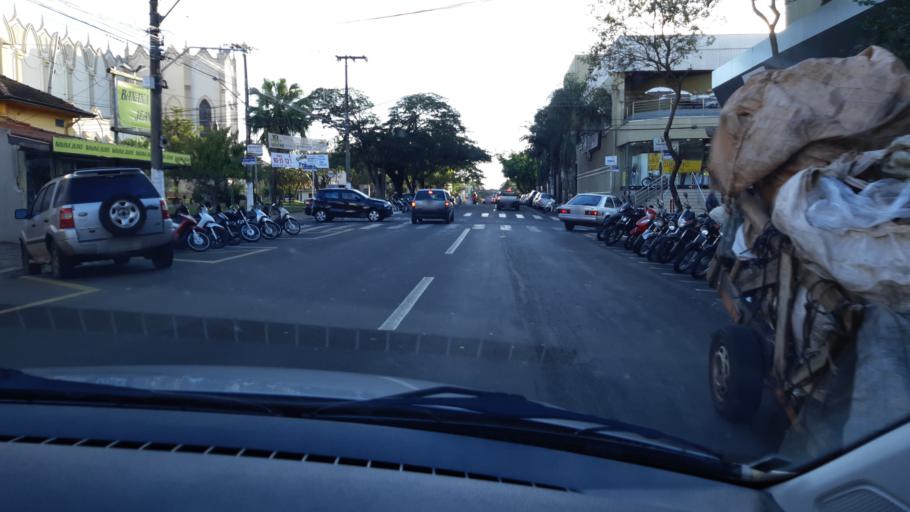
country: BR
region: Sao Paulo
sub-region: Ourinhos
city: Ourinhos
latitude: -22.9790
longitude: -49.8696
